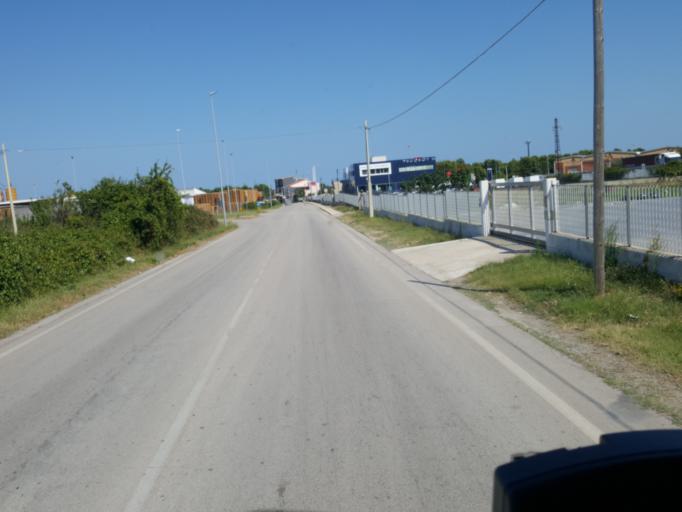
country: IT
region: Abruzzo
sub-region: Provincia di Chieti
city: Salvo Marina
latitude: 42.0597
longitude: 14.7621
